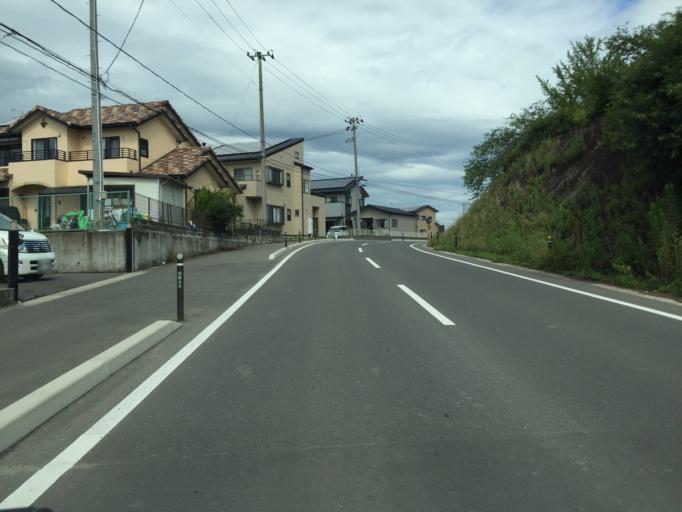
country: JP
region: Miyagi
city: Marumori
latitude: 37.8182
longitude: 140.9481
